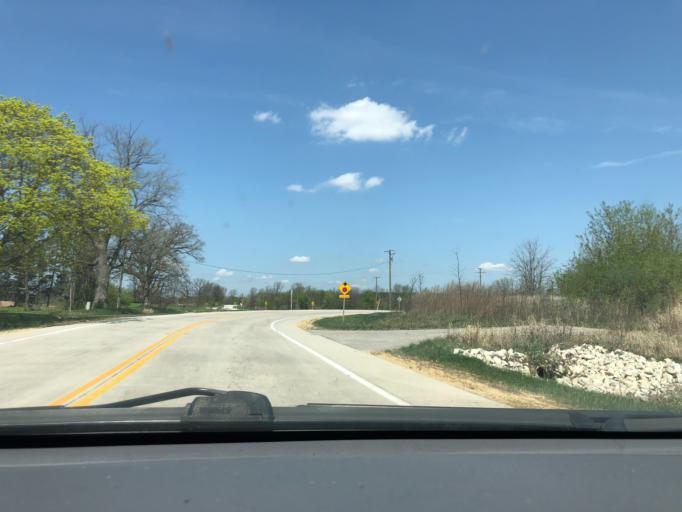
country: US
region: Illinois
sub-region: Kane County
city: Hampshire
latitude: 42.1005
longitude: -88.4827
